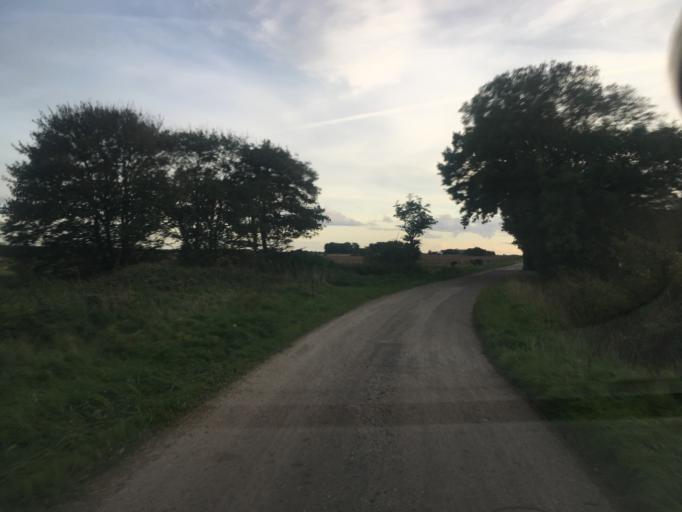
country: DK
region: South Denmark
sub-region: Tonder Kommune
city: Tonder
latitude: 54.9771
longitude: 8.9076
